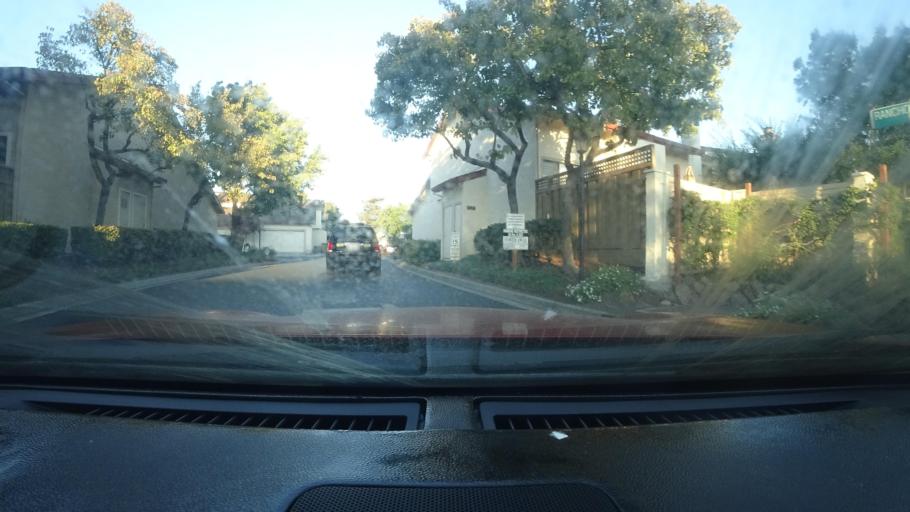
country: US
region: California
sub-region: Santa Clara County
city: Santa Clara
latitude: 37.3595
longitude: -121.9649
